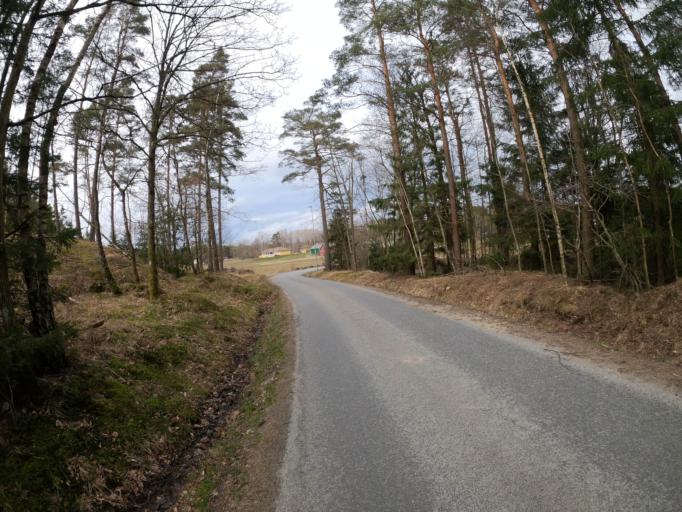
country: SE
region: Vaestra Goetaland
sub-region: Molndal
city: Kallered
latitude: 57.6197
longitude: 12.0821
